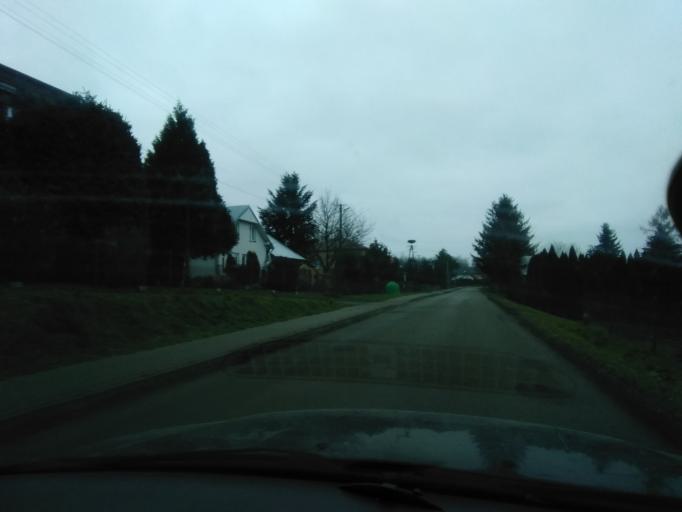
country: PL
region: Subcarpathian Voivodeship
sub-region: Powiat przeworski
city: Zarzecze
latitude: 49.9363
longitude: 22.5709
